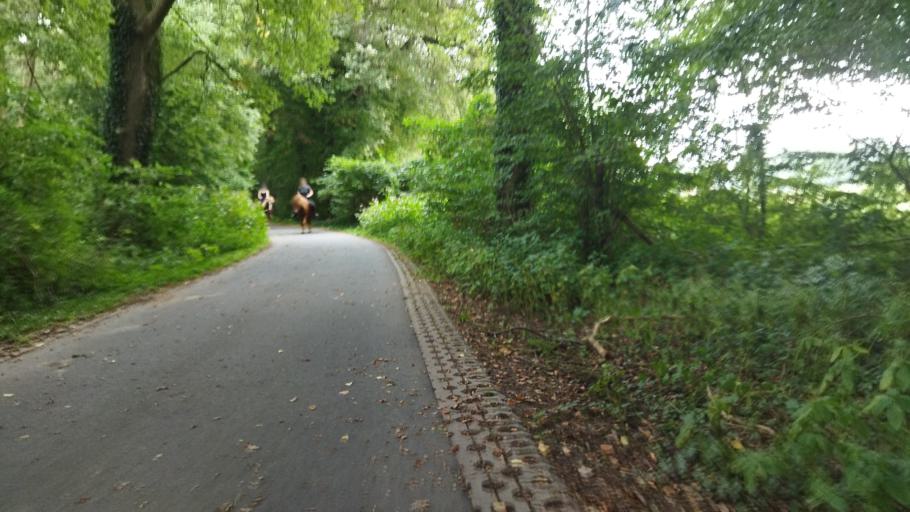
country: DE
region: North Rhine-Westphalia
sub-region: Regierungsbezirk Munster
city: Telgte
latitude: 52.0106
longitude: 7.7671
